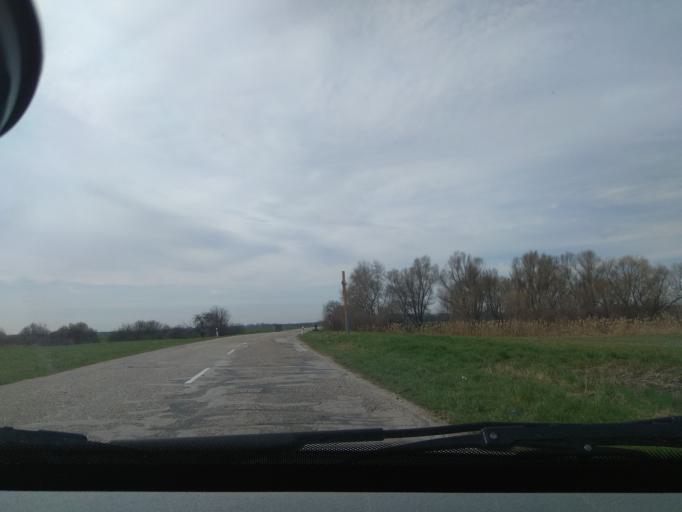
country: SK
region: Trnavsky
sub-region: Okres Dunajska Streda
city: Velky Meder
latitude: 47.8327
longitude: 17.7570
